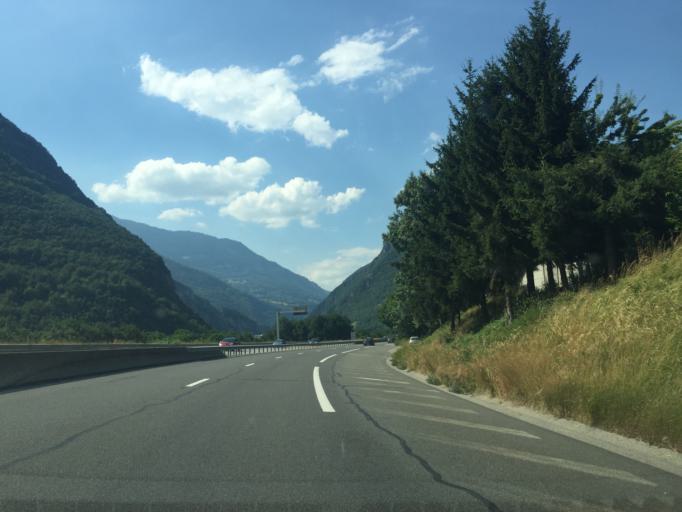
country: FR
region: Rhone-Alpes
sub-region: Departement de la Savoie
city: Aigueblanche
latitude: 45.5157
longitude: 6.4875
